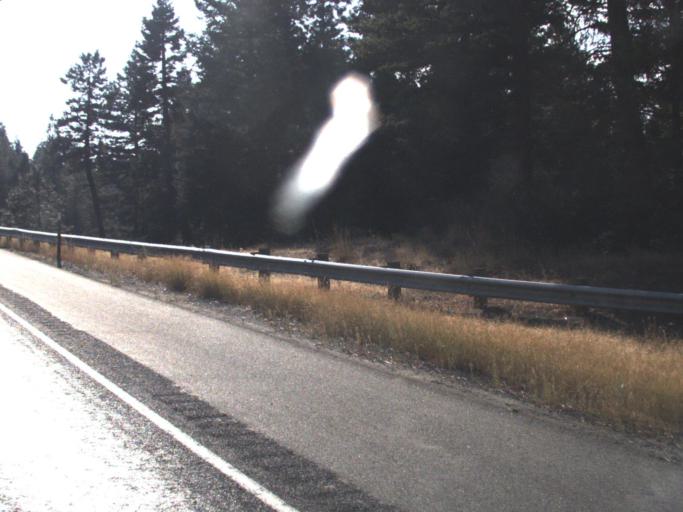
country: US
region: Washington
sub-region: Pend Oreille County
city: Newport
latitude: 48.1344
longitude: -117.1714
